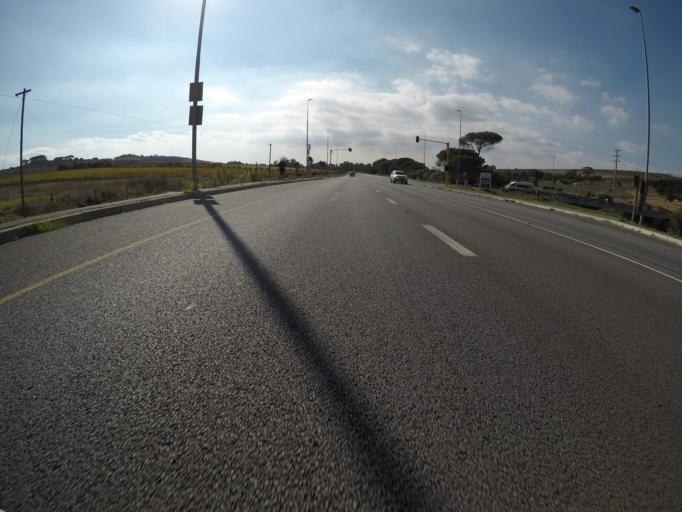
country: ZA
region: Western Cape
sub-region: Cape Winelands District Municipality
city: Stellenbosch
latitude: -33.9025
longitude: 18.8403
